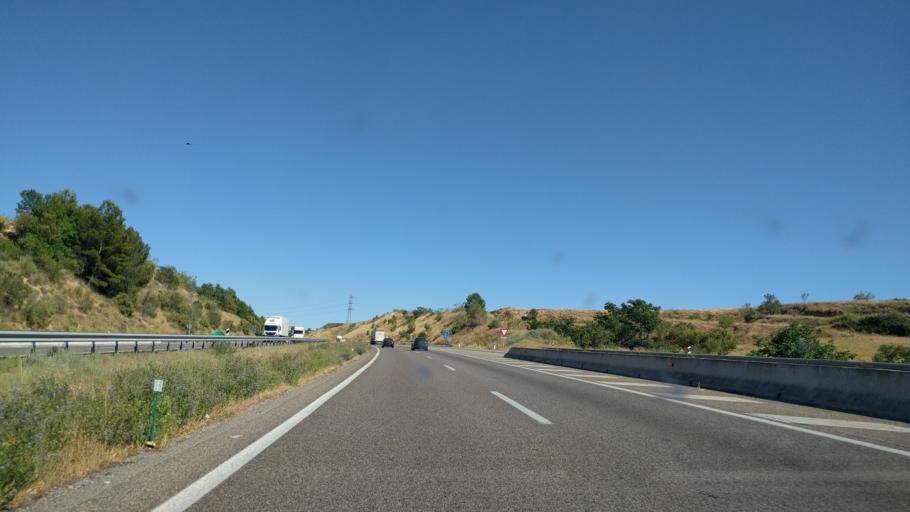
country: ES
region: Catalonia
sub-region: Provincia de Lleida
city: Alcoletge
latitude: 41.6394
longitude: 0.6783
